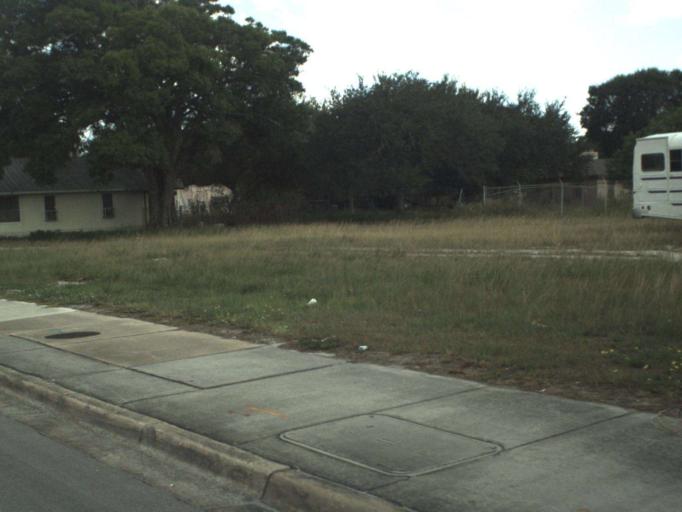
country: US
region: Florida
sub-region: Saint Lucie County
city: Fort Pierce
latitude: 27.4473
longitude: -80.3416
